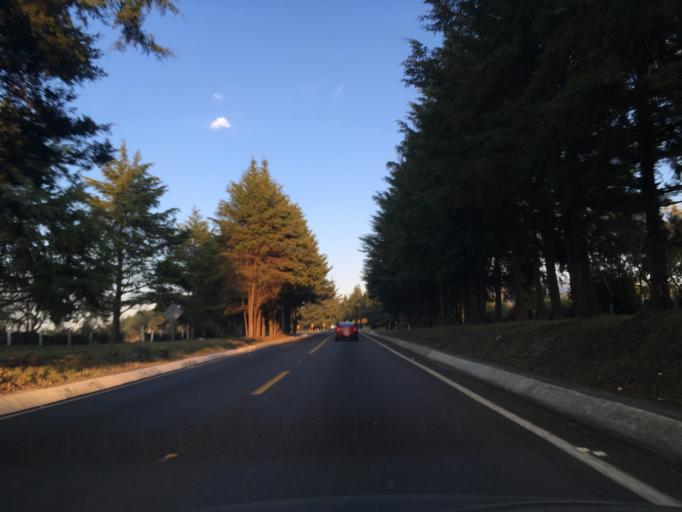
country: MX
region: Michoacan
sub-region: Patzcuaro
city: Santa Ana Chapitiro
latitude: 19.5129
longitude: -101.6703
